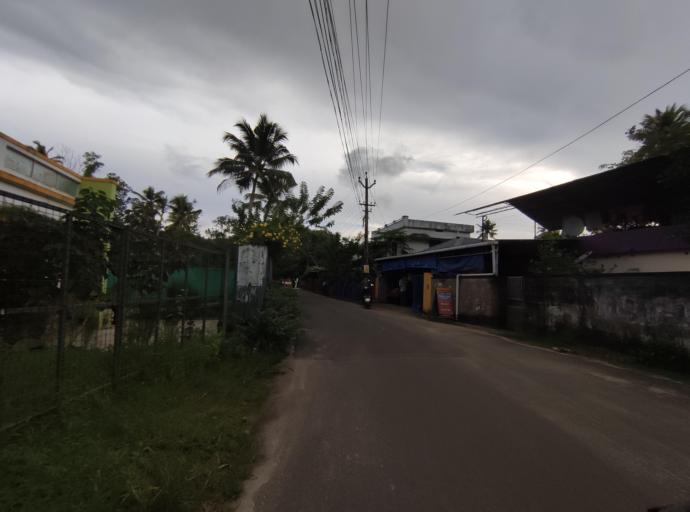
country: IN
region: Kerala
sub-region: Alappuzha
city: Shertallai
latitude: 9.6696
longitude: 76.3431
